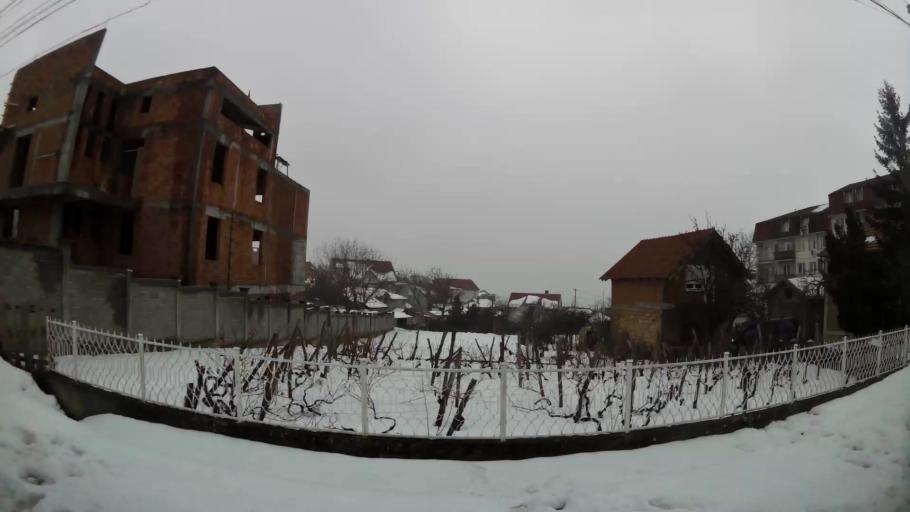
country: RS
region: Central Serbia
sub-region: Belgrade
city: Zvezdara
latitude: 44.7469
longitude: 20.5161
